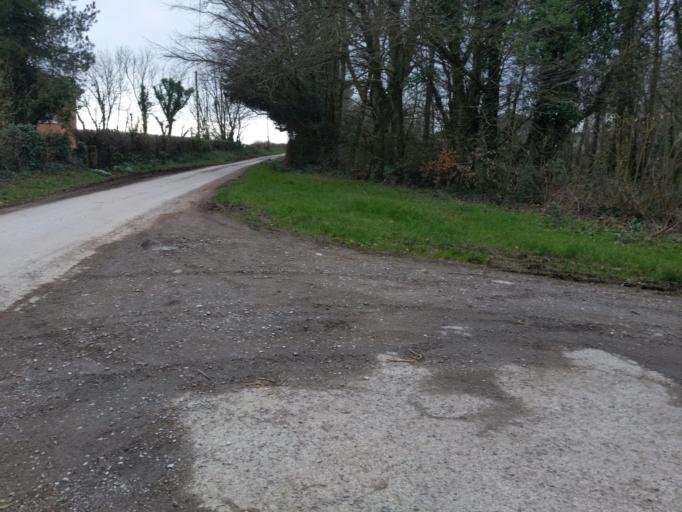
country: GB
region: England
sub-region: Devon
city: Yelverton
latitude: 50.4587
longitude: -4.1251
